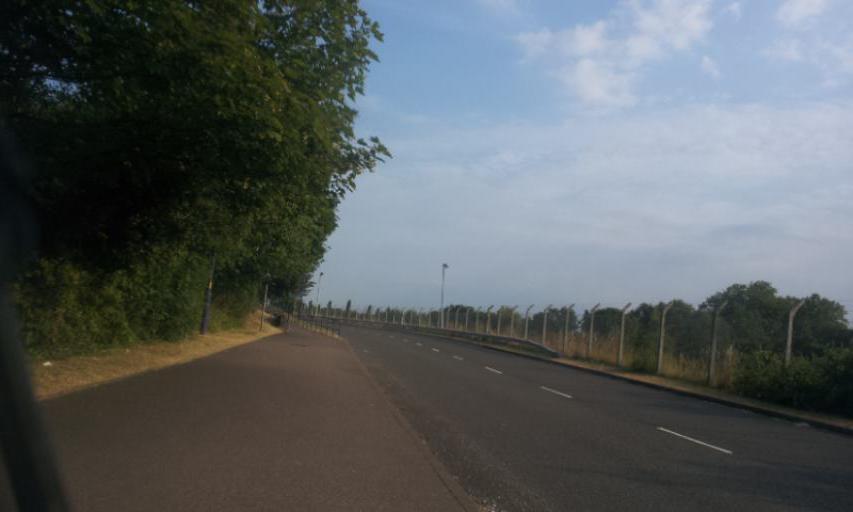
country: GB
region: England
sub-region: Kent
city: Dartford
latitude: 51.4424
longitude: 0.2228
